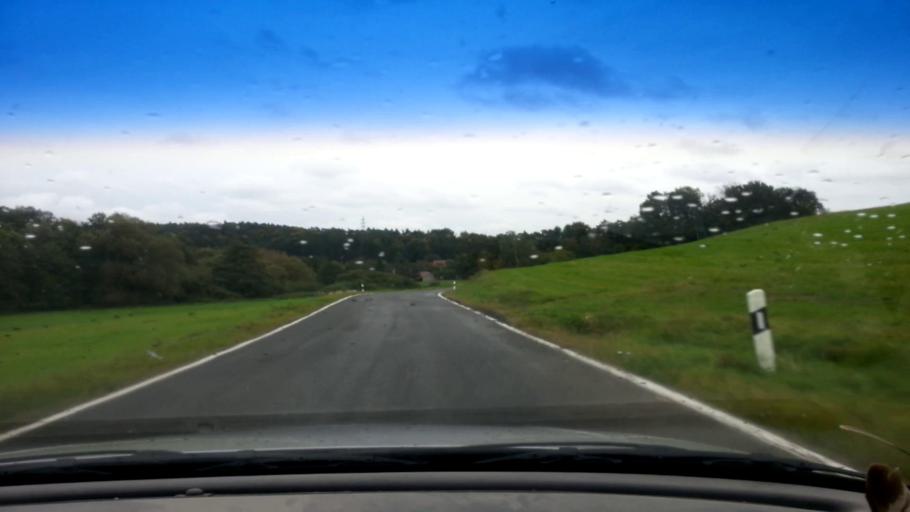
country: DE
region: Bavaria
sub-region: Regierungsbezirk Unterfranken
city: Kirchlauter
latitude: 50.0281
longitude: 10.7327
